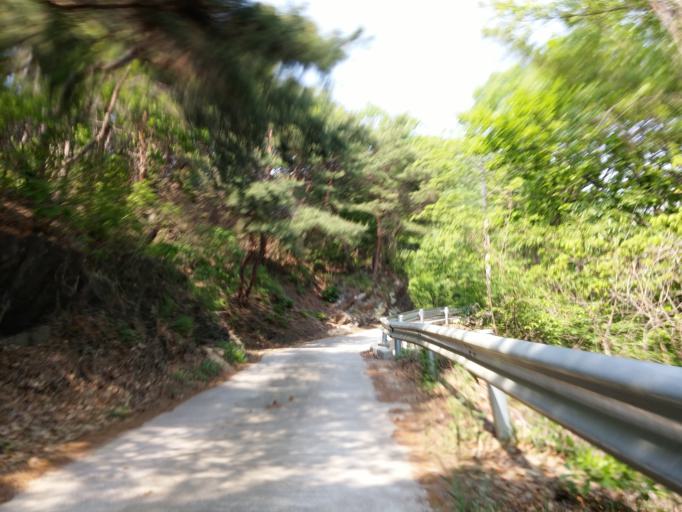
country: KR
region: Chungcheongbuk-do
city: Okcheon
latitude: 36.3769
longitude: 127.6044
